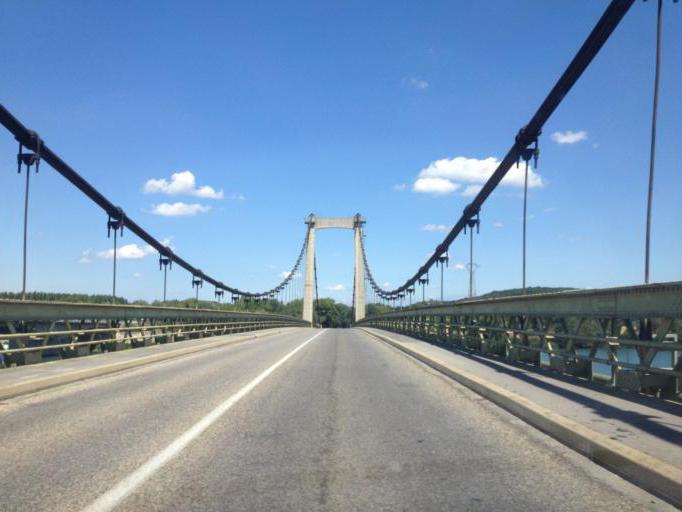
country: FR
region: Languedoc-Roussillon
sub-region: Departement du Gard
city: Montfaucon
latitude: 44.0710
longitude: 4.7685
